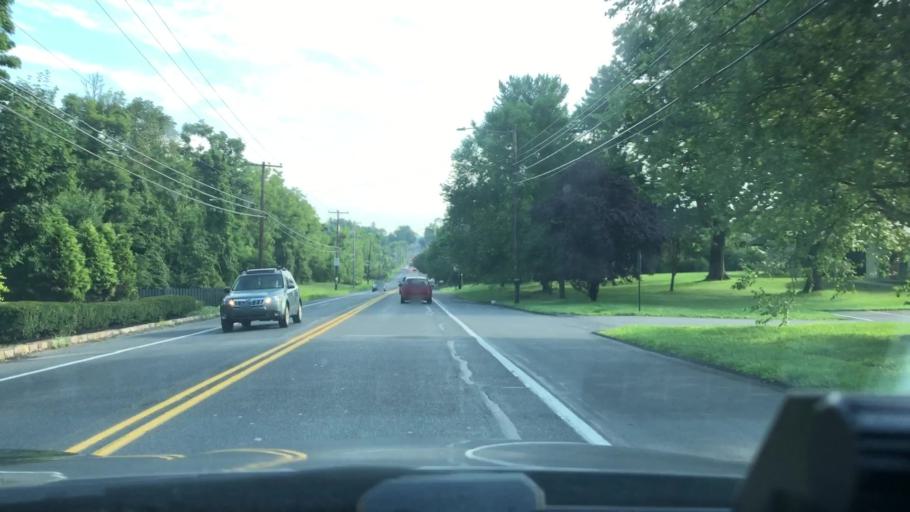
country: US
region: Pennsylvania
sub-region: Northampton County
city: Middletown
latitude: 40.6646
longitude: -75.3509
